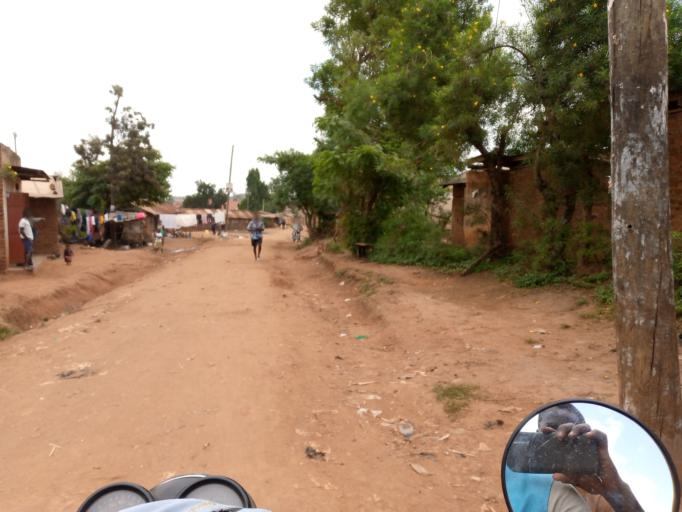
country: UG
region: Eastern Region
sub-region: Mbale District
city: Mbale
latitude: 1.0852
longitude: 34.1658
